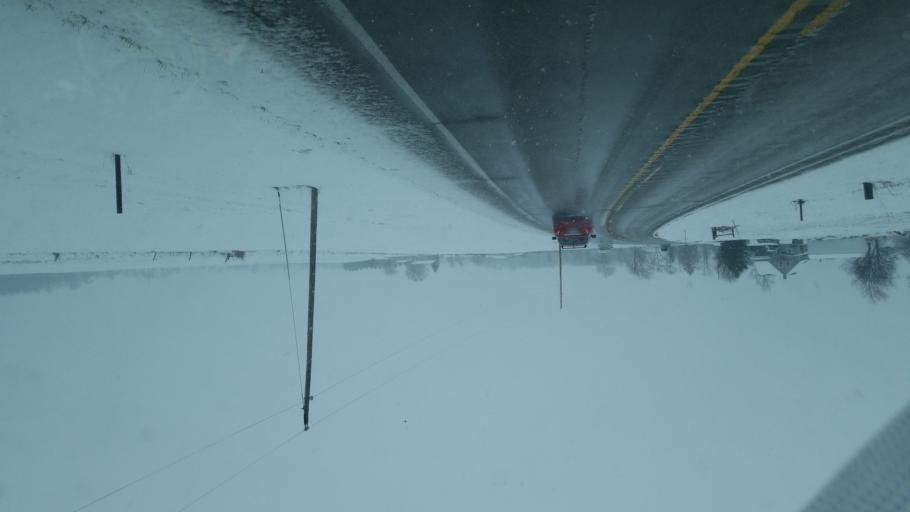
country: US
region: Indiana
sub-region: Randolph County
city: Parker City
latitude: 40.0658
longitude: -85.2623
